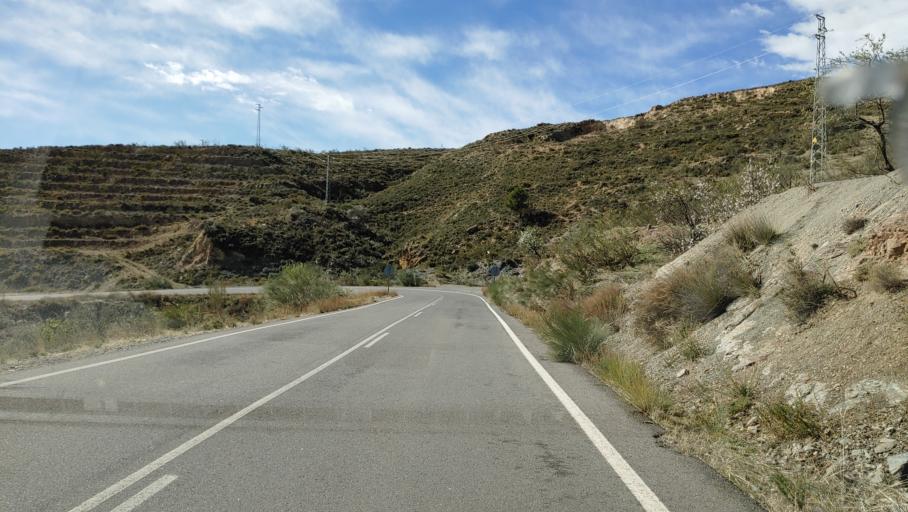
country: ES
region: Andalusia
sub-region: Provincia de Almeria
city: Ohanes
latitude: 37.0360
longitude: -2.7330
